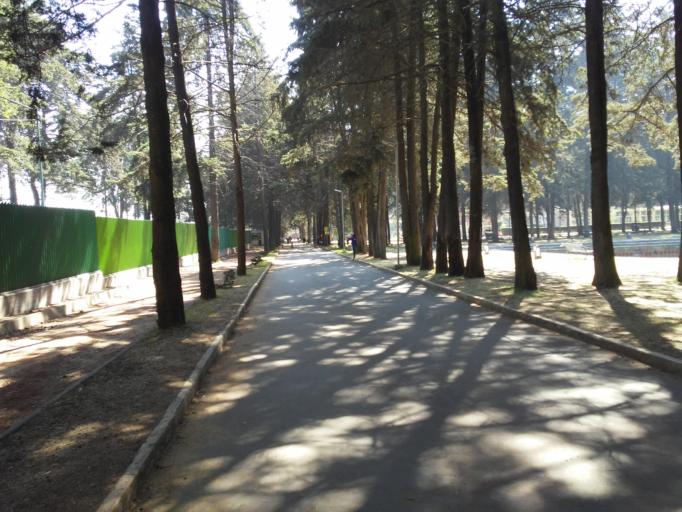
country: MX
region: Mexico
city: Toluca
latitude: 19.2719
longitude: -99.6517
